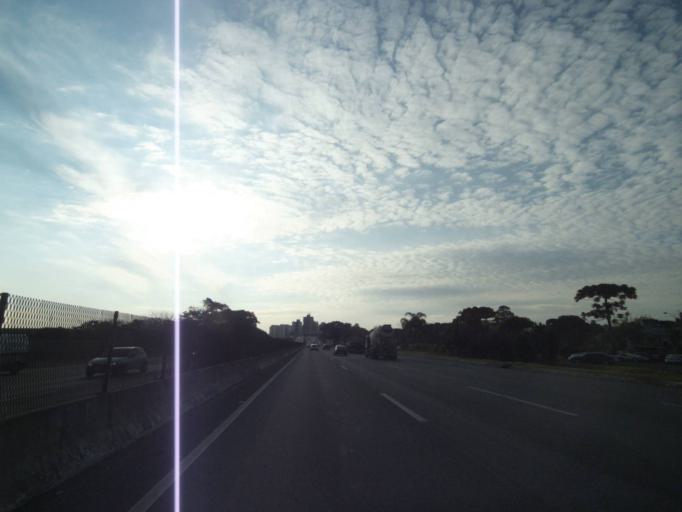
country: BR
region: Parana
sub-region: Pinhais
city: Pinhais
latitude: -25.4472
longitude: -49.2299
